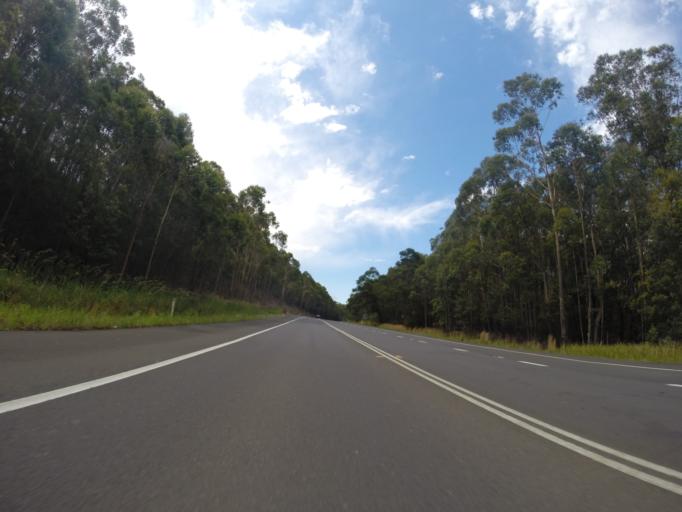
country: AU
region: New South Wales
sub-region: Shoalhaven Shire
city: Milton
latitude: -35.1906
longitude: 150.4367
